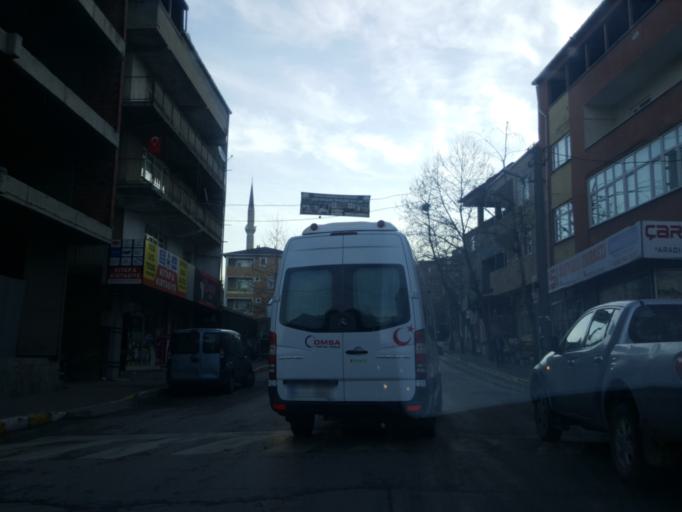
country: TR
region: Kocaeli
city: Tavsancil
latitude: 40.7904
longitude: 29.5421
